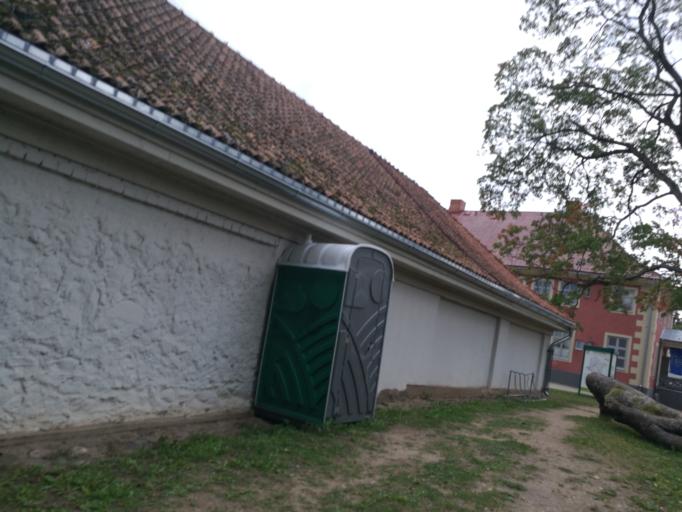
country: LV
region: Limbazu Rajons
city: Limbazi
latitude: 57.5159
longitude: 24.7129
